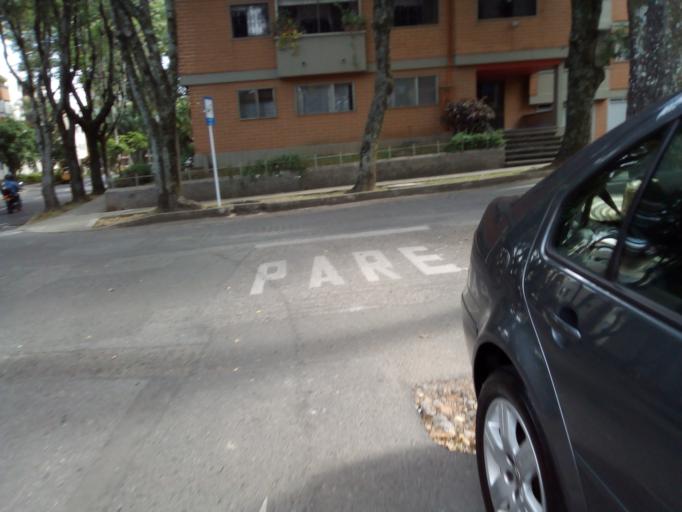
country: CO
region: Antioquia
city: Medellin
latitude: 6.2674
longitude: -75.5934
